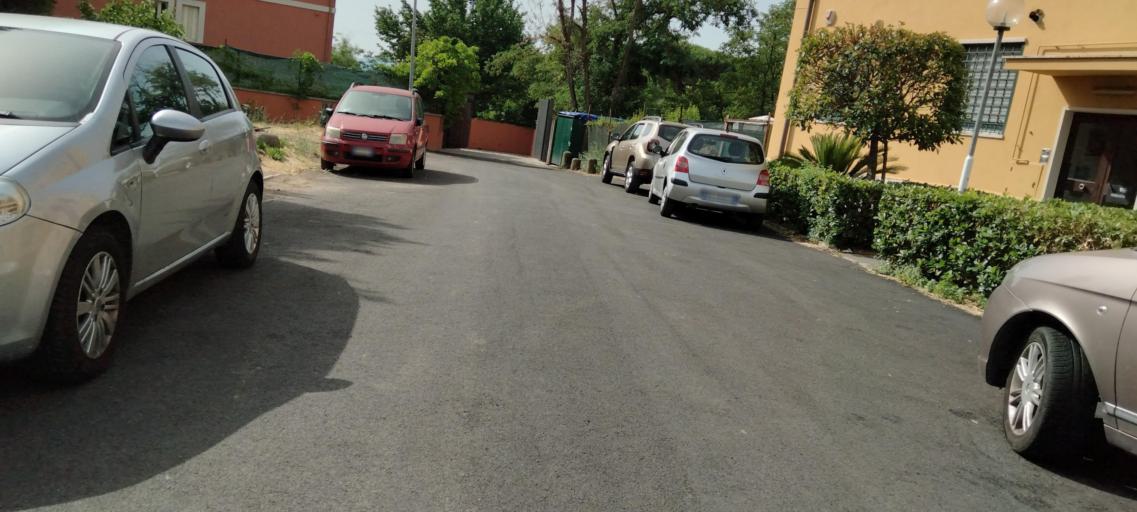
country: IT
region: Latium
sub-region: Citta metropolitana di Roma Capitale
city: Colle Verde
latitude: 41.9354
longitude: 12.5839
